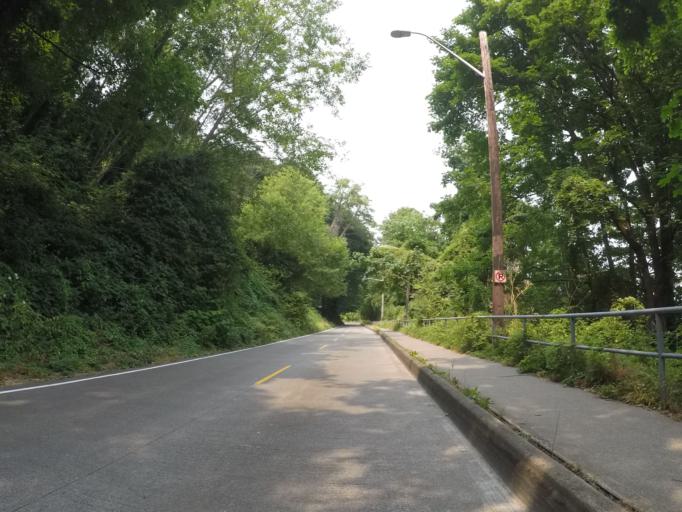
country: US
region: Washington
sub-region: King County
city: Seattle
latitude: 47.5918
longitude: -122.3835
